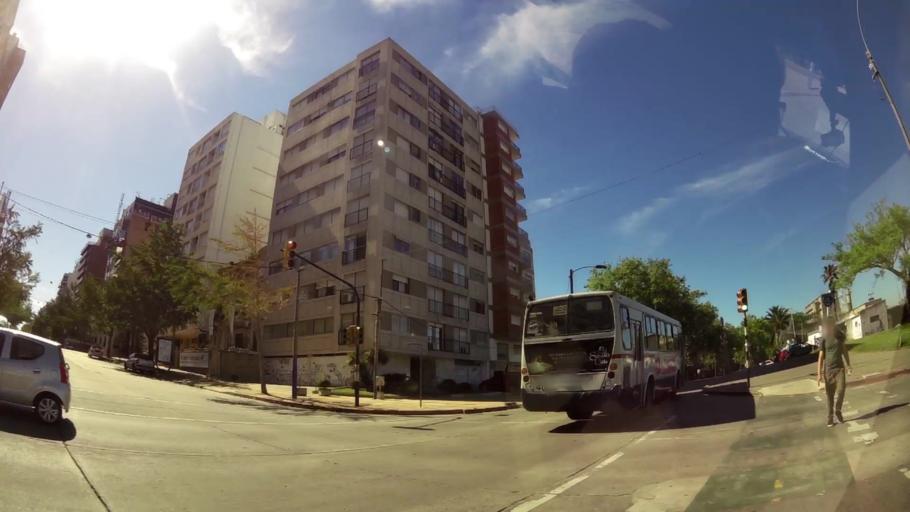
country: UY
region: Montevideo
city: Montevideo
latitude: -34.9150
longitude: -56.1574
